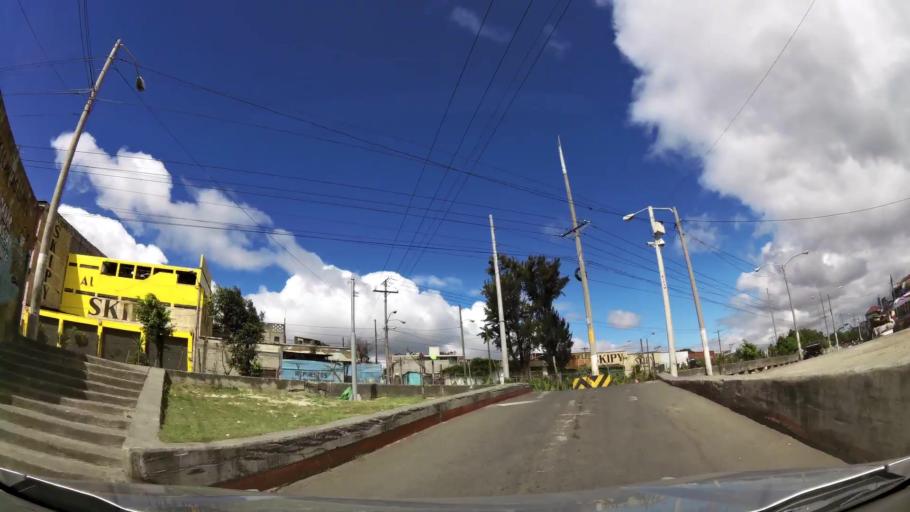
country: GT
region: Guatemala
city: Guatemala City
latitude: 14.6135
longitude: -90.5253
